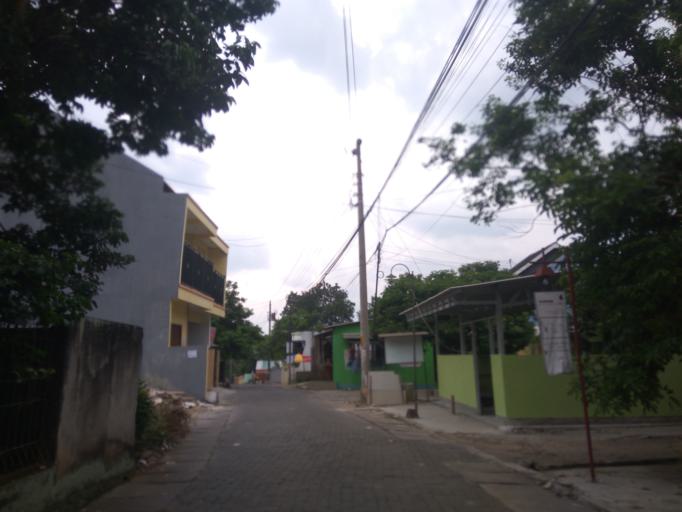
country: ID
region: Central Java
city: Semarang
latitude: -7.0642
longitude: 110.4412
